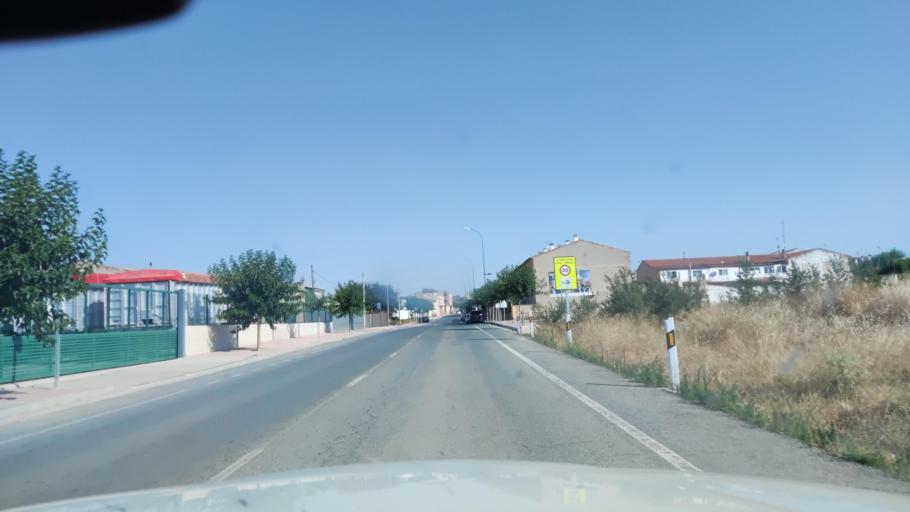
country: ES
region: Castille-La Mancha
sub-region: Provincia de Albacete
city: Pozo-Canada
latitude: 38.8074
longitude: -1.7355
